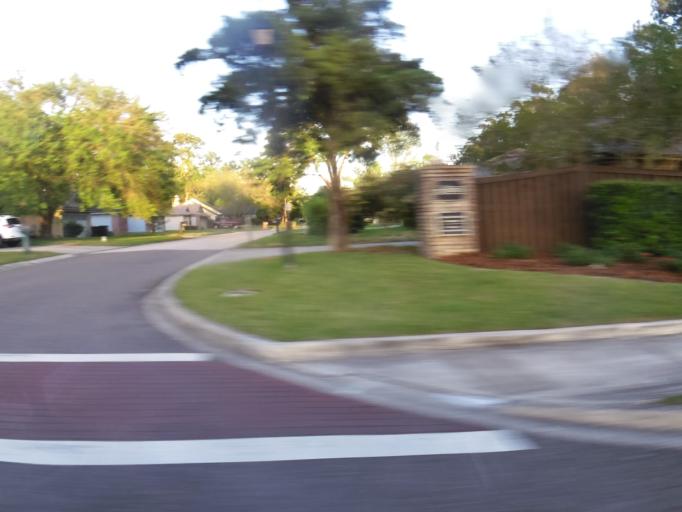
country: US
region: Florida
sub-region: Duval County
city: Jacksonville
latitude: 30.2712
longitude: -81.5711
